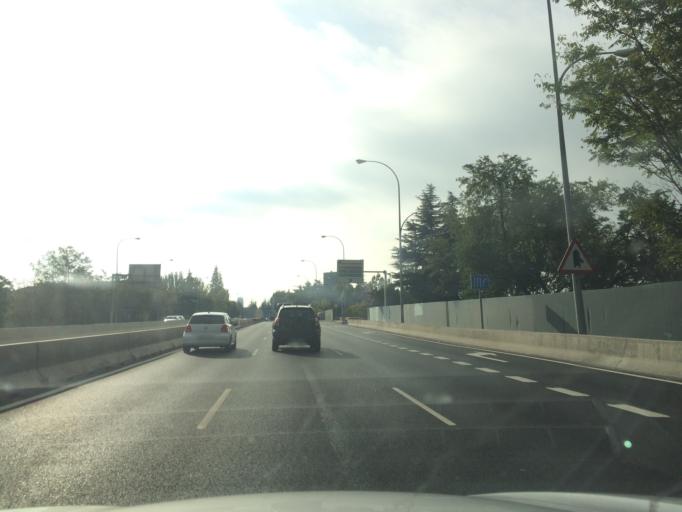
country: ES
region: Madrid
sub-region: Provincia de Madrid
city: Moncloa-Aravaca
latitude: 40.4450
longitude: -3.7330
